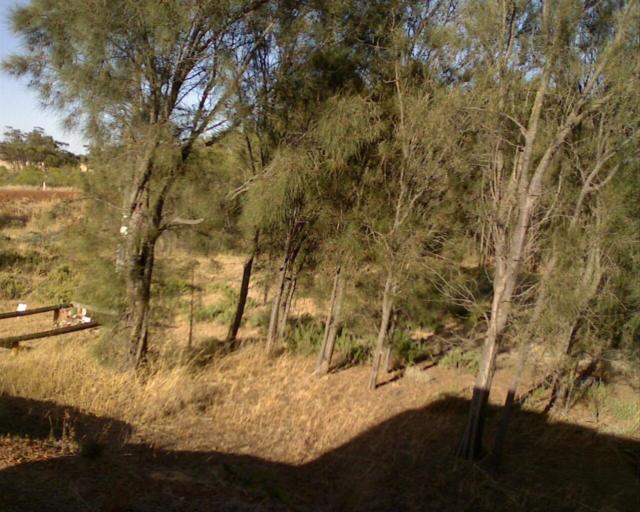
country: AU
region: Western Australia
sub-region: Moora
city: Moora
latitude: -30.2806
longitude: 116.0581
